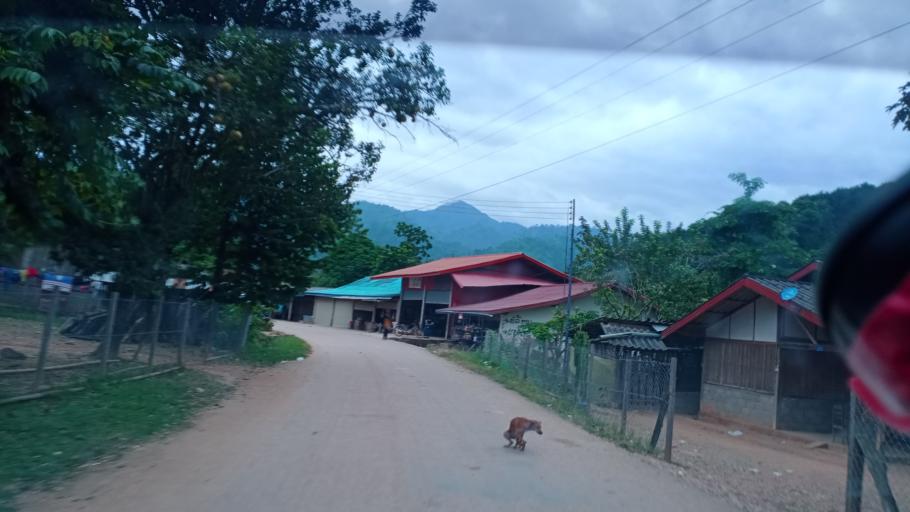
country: TH
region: Changwat Bueng Kan
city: Pak Khat
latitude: 18.7126
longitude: 103.2120
